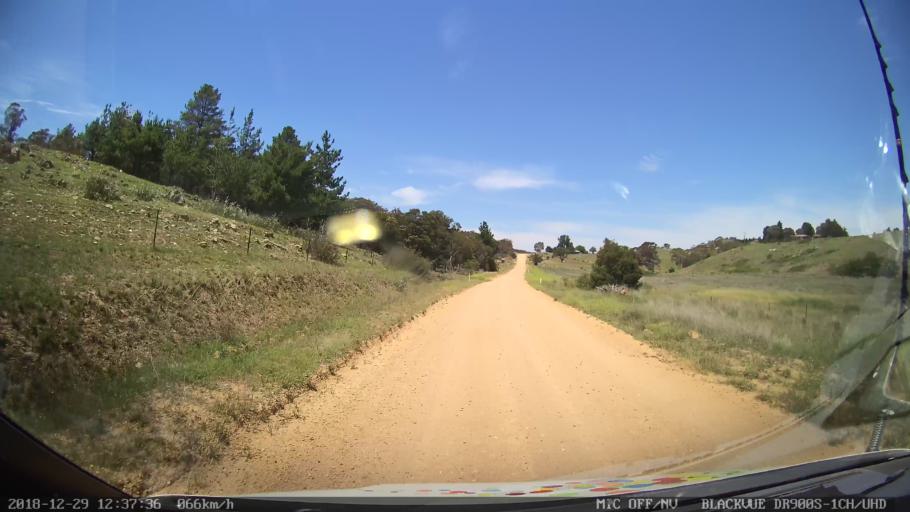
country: AU
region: Australian Capital Territory
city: Macarthur
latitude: -35.5815
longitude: 149.2286
